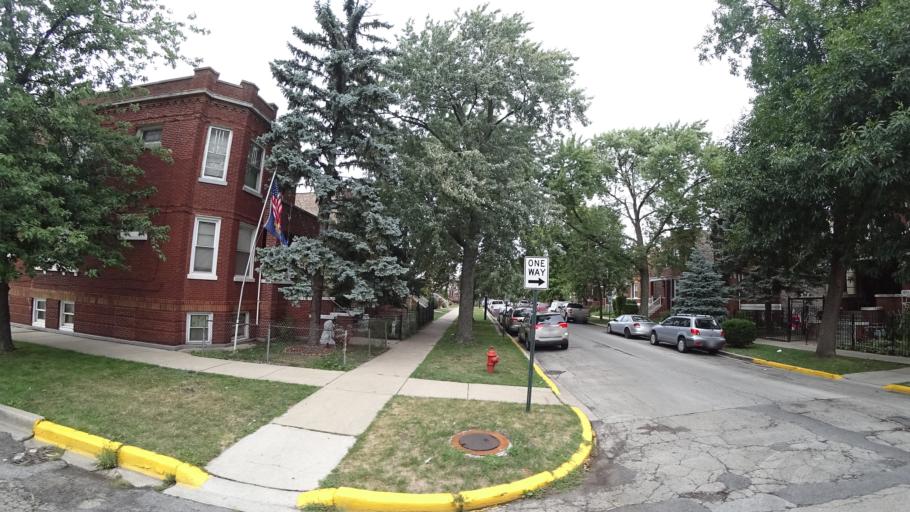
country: US
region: Illinois
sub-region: Cook County
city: Cicero
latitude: 41.8528
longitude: -87.7653
